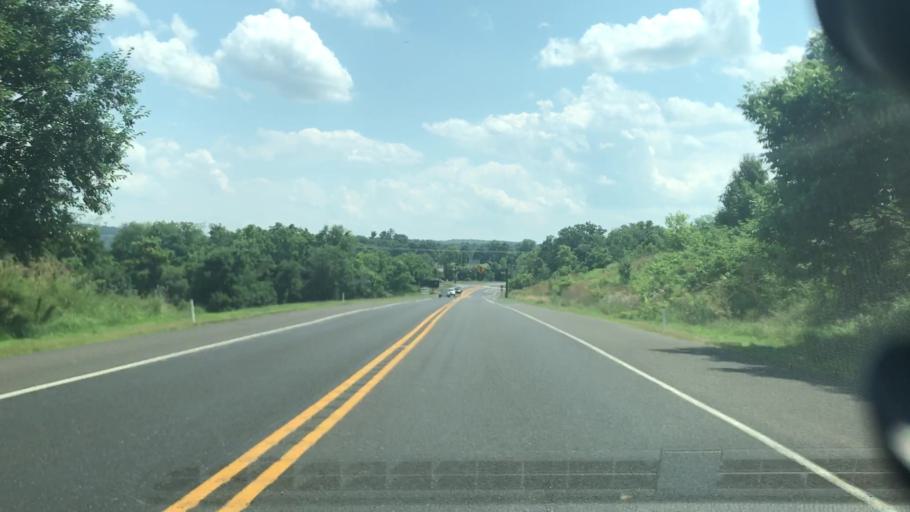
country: US
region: Pennsylvania
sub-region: Bucks County
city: New Hope
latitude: 40.3745
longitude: -74.9640
